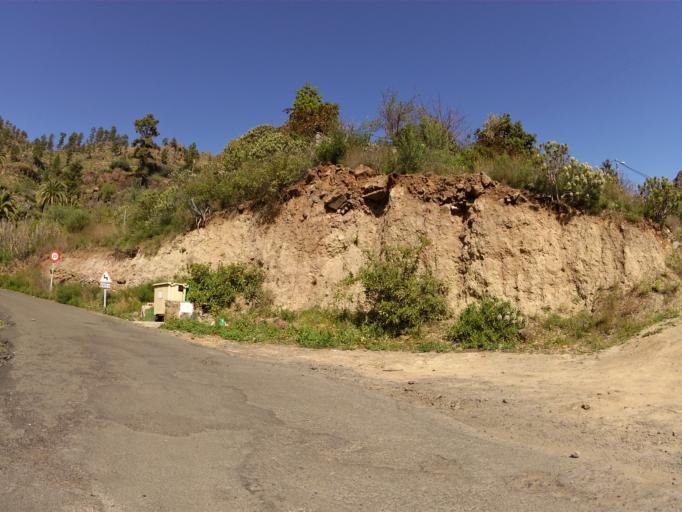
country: ES
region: Canary Islands
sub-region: Provincia de Las Palmas
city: Mogan
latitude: 27.8983
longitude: -15.6818
